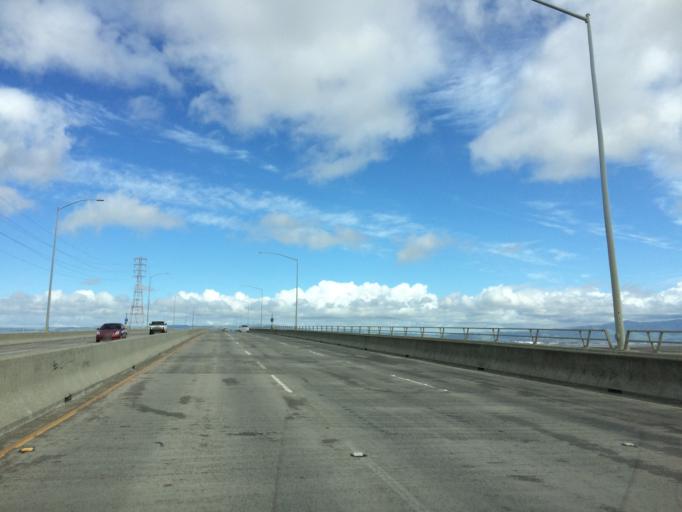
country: US
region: California
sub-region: San Mateo County
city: East Palo Alto
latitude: 37.5035
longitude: -122.1220
